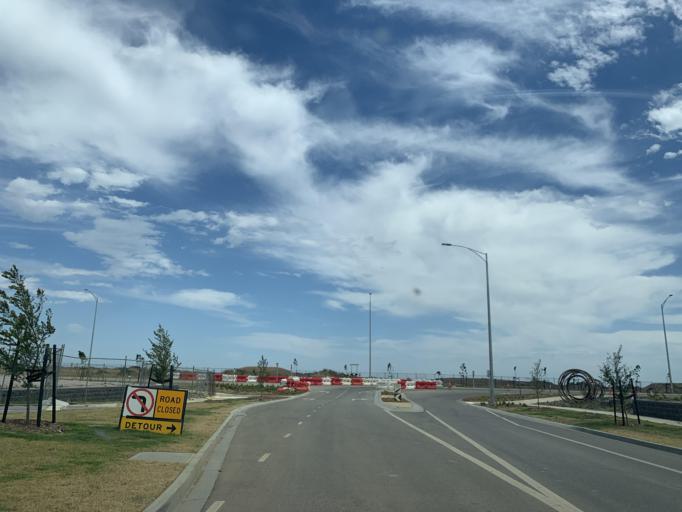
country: AU
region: Victoria
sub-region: Cardinia
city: Officer South
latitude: -38.1234
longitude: 145.3707
